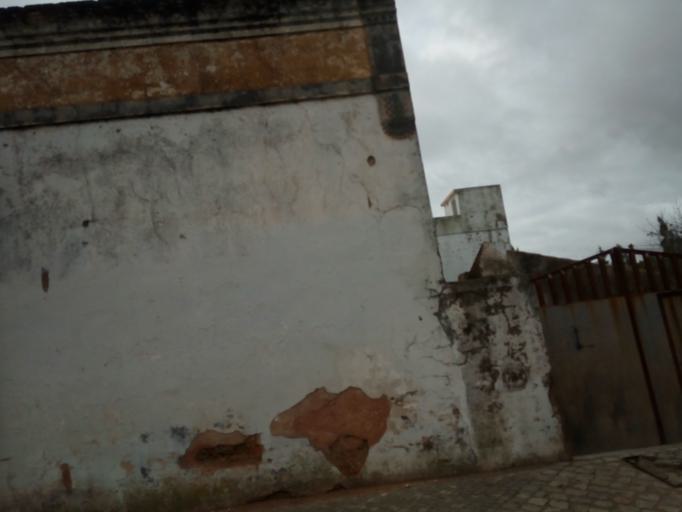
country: PT
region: Faro
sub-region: Loule
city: Loule
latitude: 37.1332
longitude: -8.0090
